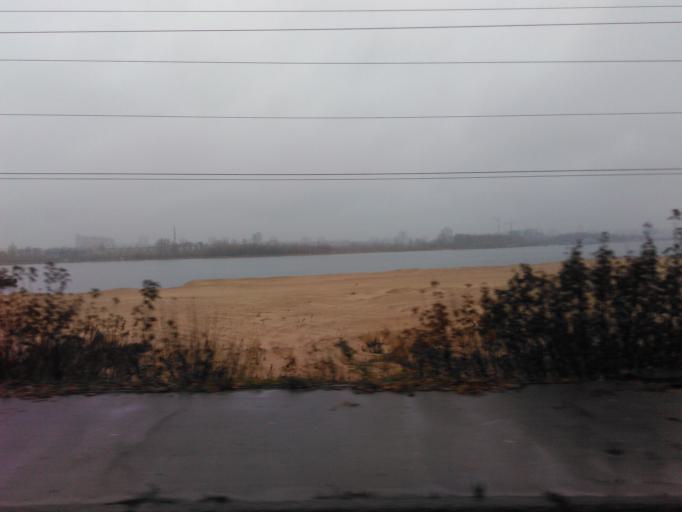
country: RU
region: Tatarstan
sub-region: Gorod Kazan'
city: Kazan
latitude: 55.7977
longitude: 49.0807
